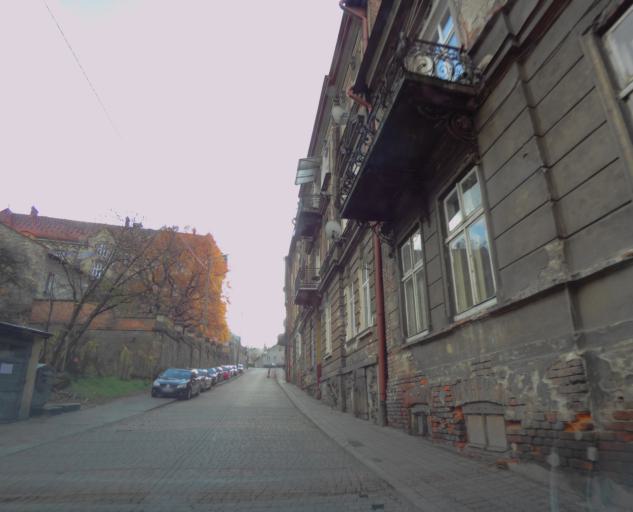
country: PL
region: Subcarpathian Voivodeship
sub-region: Przemysl
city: Przemysl
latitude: 49.7810
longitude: 22.7746
